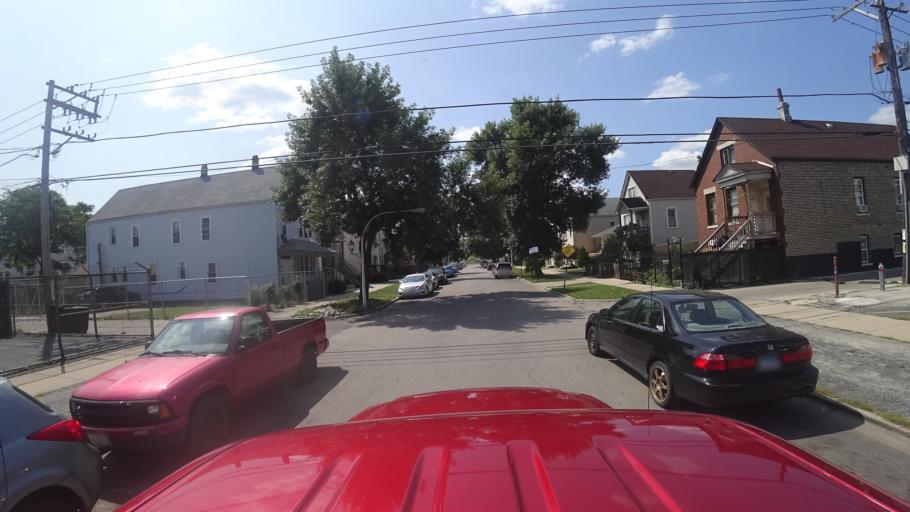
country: US
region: Illinois
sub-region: Cook County
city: Chicago
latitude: 41.8081
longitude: -87.6881
